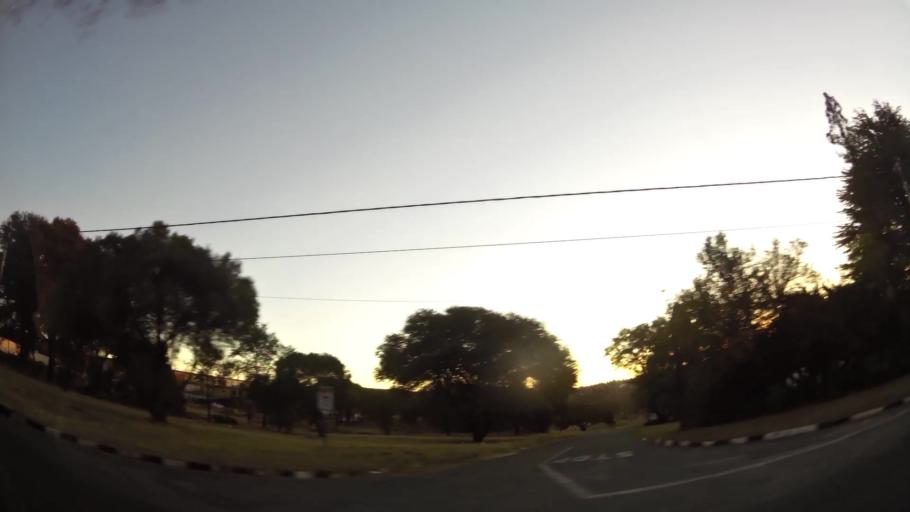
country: ZA
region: Gauteng
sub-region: City of Johannesburg Metropolitan Municipality
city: Roodepoort
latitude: -26.1620
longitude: 27.9124
